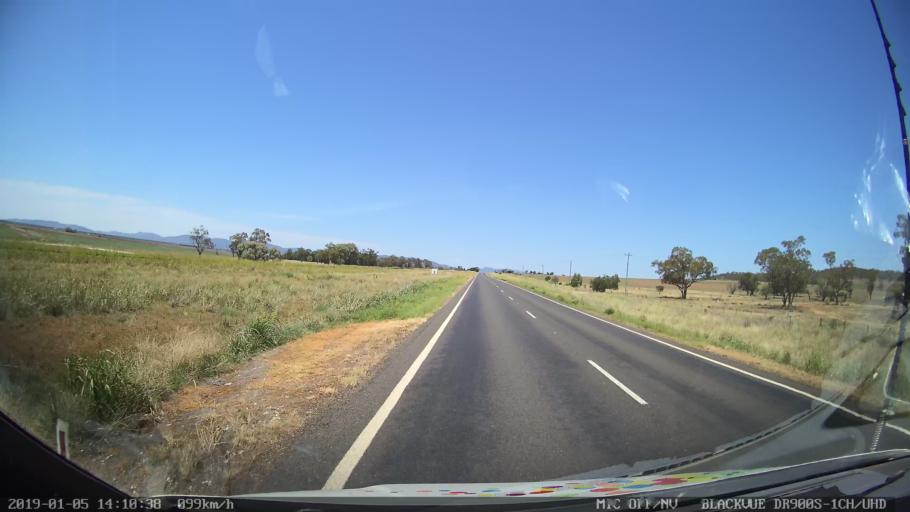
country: AU
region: New South Wales
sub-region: Gunnedah
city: Gunnedah
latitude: -31.2454
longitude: 150.4458
